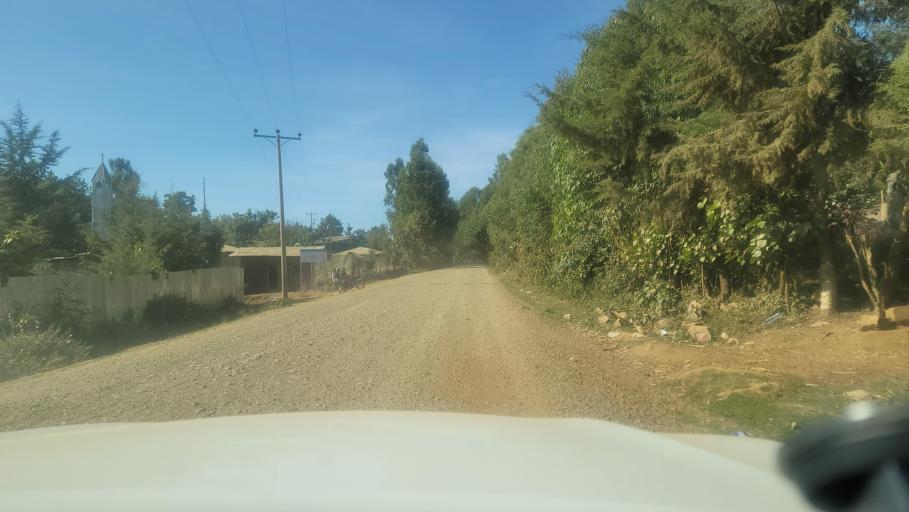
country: ET
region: Oromiya
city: Agaro
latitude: 7.8061
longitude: 36.5016
